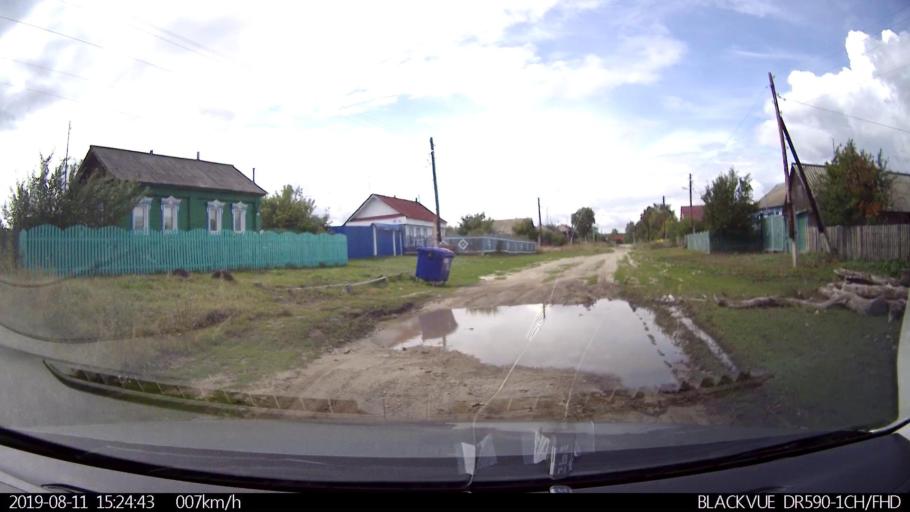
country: RU
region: Ulyanovsk
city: Ignatovka
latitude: 53.8485
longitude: 47.5778
